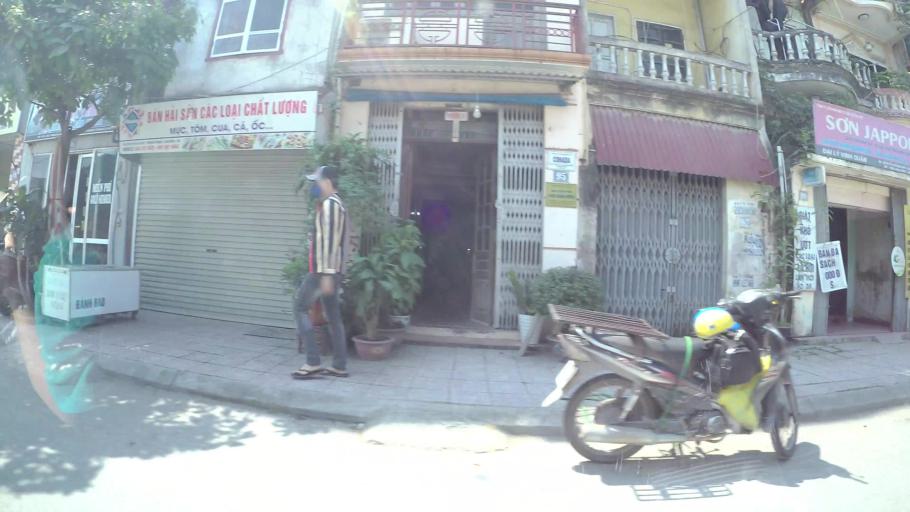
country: VN
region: Ha Noi
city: Hoan Kiem
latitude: 21.0536
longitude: 105.8778
